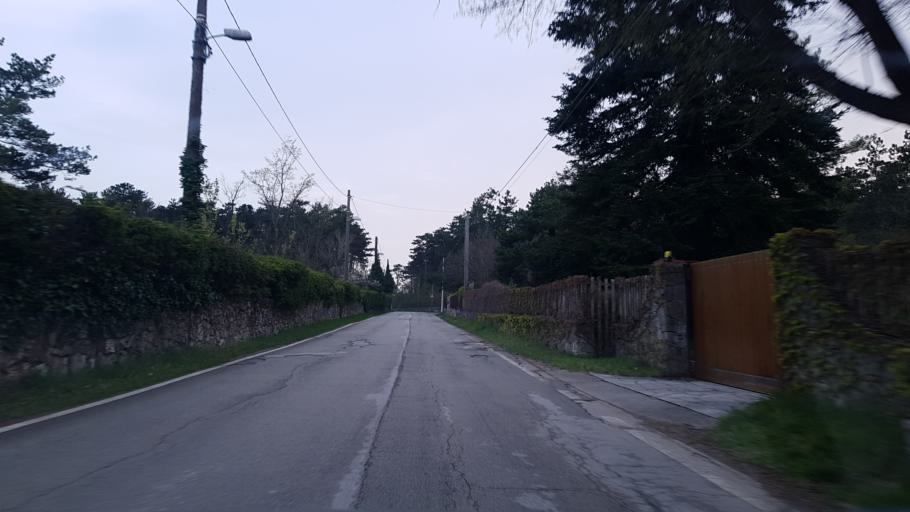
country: IT
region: Friuli Venezia Giulia
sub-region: Provincia di Trieste
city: Domio
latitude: 45.6501
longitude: 13.8394
